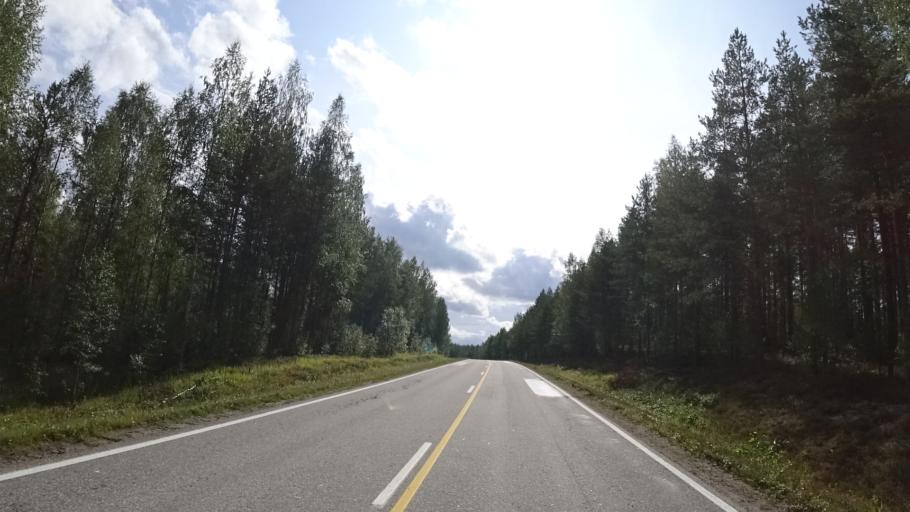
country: FI
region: North Karelia
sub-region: Joensuu
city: Ilomantsi
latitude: 62.6947
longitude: 30.9856
